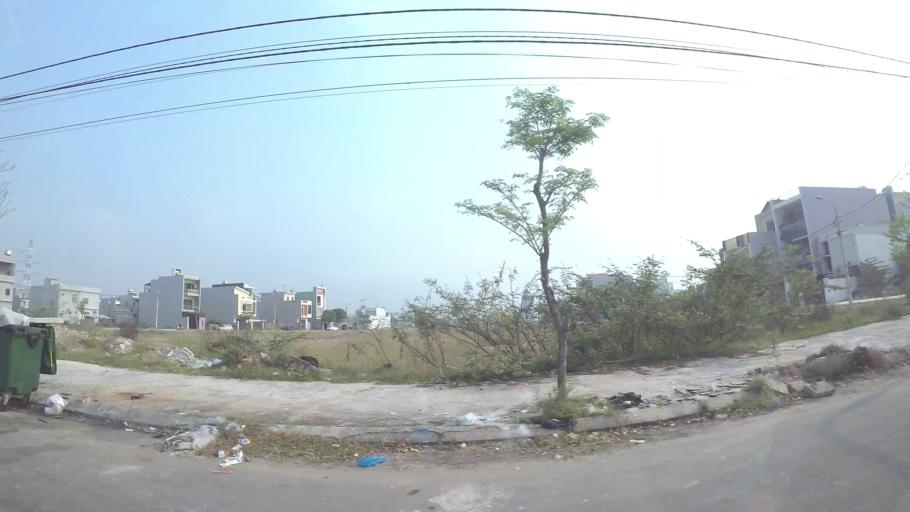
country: VN
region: Da Nang
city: Cam Le
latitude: 16.0090
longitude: 108.2256
